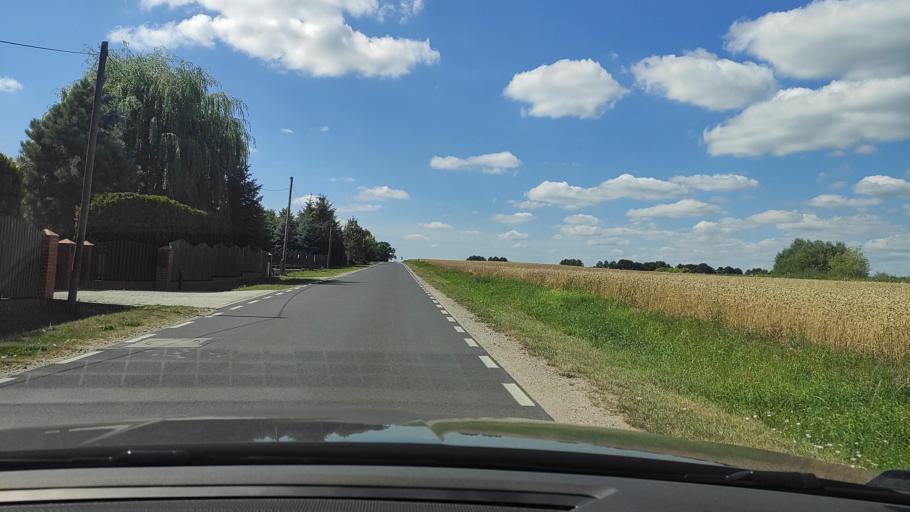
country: PL
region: Greater Poland Voivodeship
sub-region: Powiat poznanski
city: Kostrzyn
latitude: 52.4797
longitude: 17.1774
